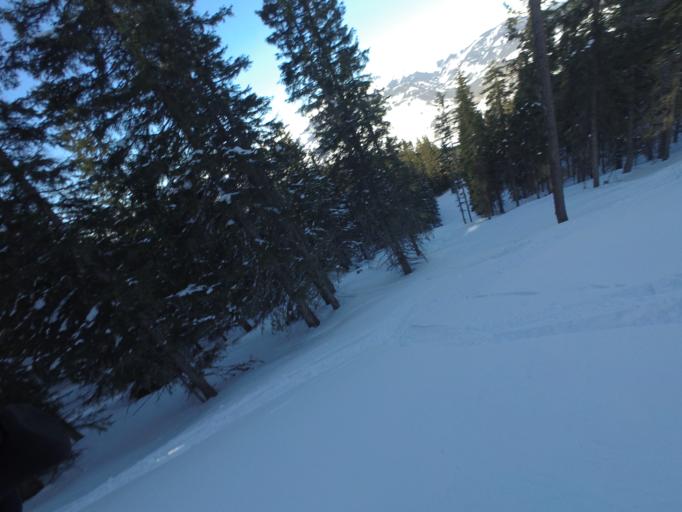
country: AT
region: Salzburg
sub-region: Politischer Bezirk Zell am See
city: Lend
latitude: 47.2699
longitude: 13.0193
